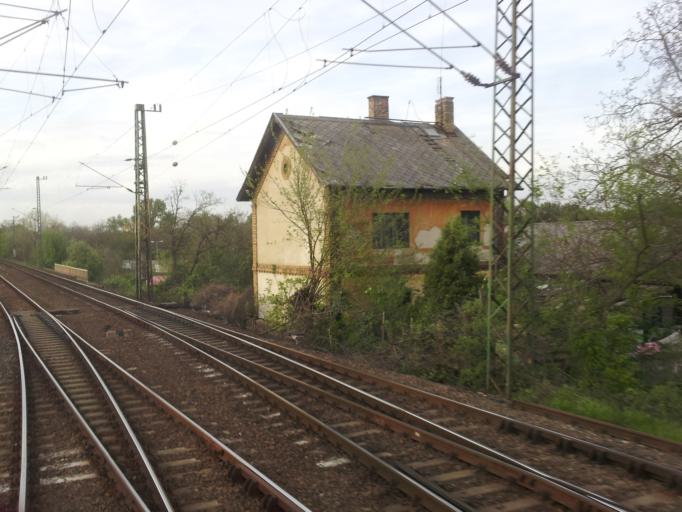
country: HU
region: Budapest
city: Budapest X. keruelet
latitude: 47.4959
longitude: 19.1593
